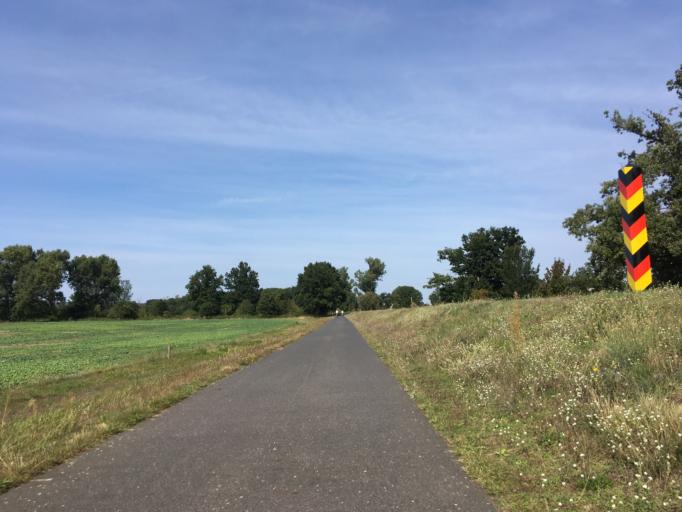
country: DE
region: Brandenburg
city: Guben
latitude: 51.9959
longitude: 14.7199
